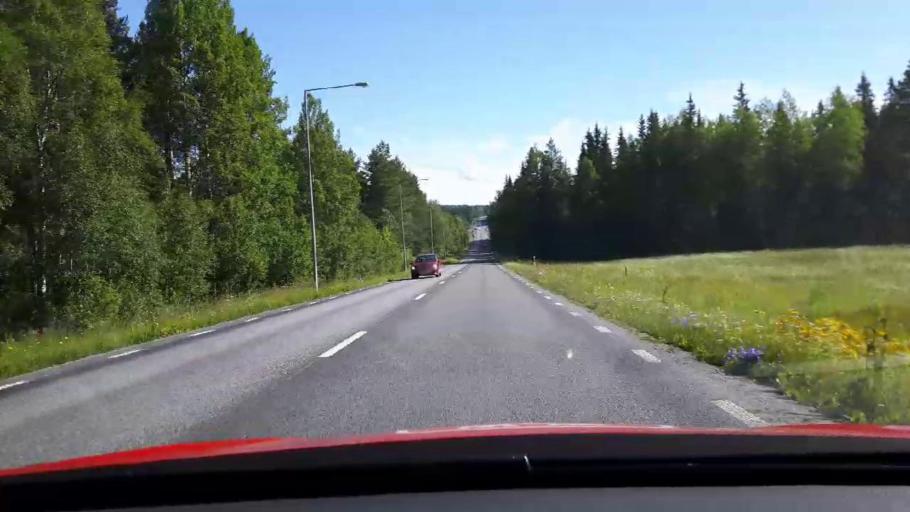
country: SE
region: Jaemtland
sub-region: OEstersunds Kommun
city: Ostersund
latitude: 63.1968
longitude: 14.6676
